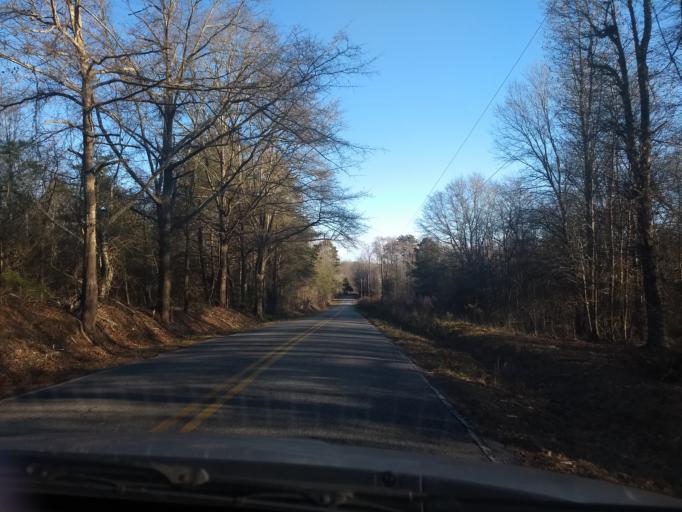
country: US
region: South Carolina
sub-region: Greenville County
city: Greer
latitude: 35.0115
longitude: -82.2093
